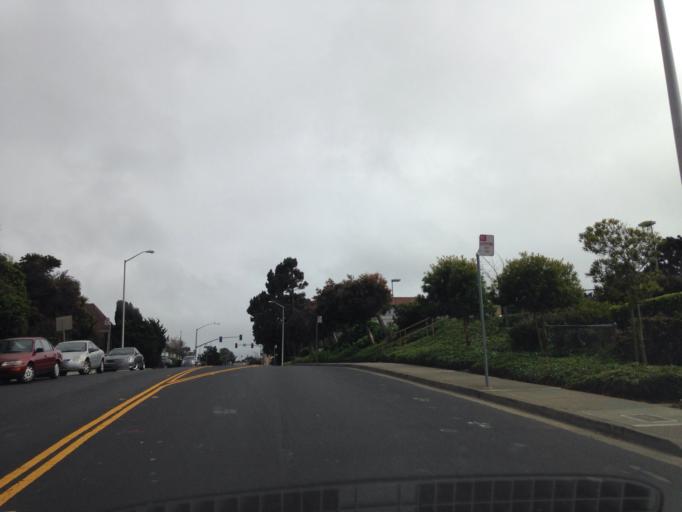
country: US
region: California
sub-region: San Mateo County
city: Broadmoor
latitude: 37.6895
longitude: -122.4723
